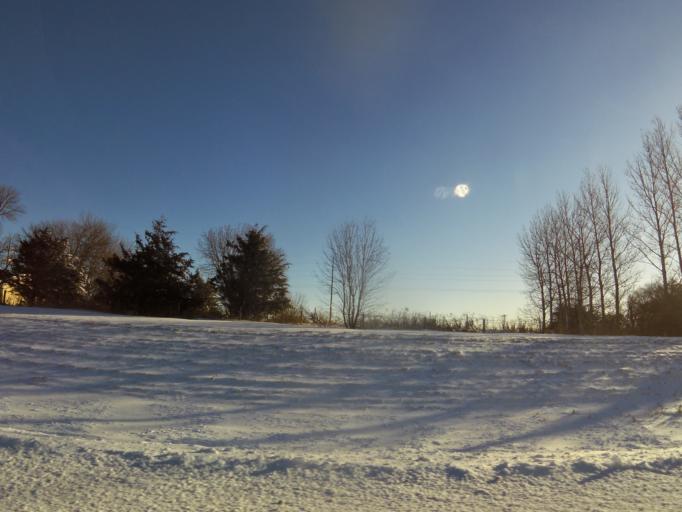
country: US
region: Minnesota
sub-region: Steele County
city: Owatonna
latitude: 44.0361
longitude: -93.2476
